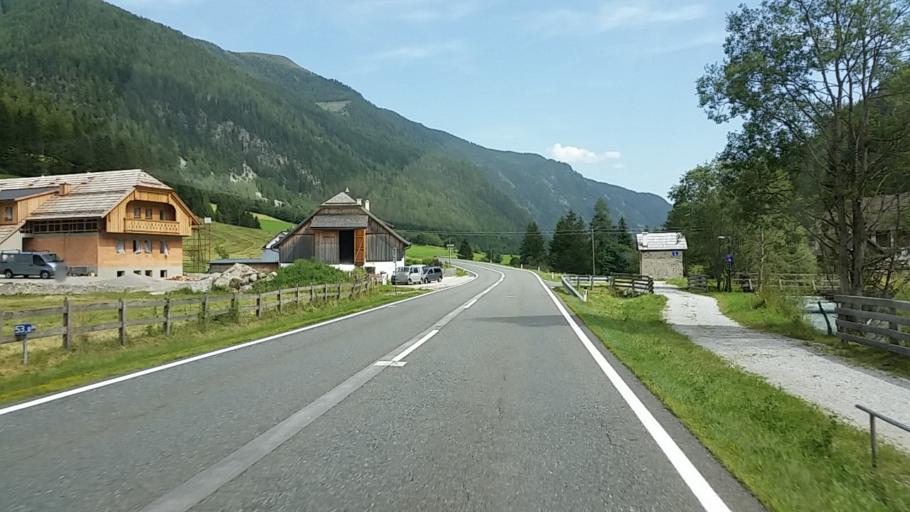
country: AT
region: Salzburg
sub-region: Politischer Bezirk Tamsweg
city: Tweng
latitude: 47.1848
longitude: 13.6131
